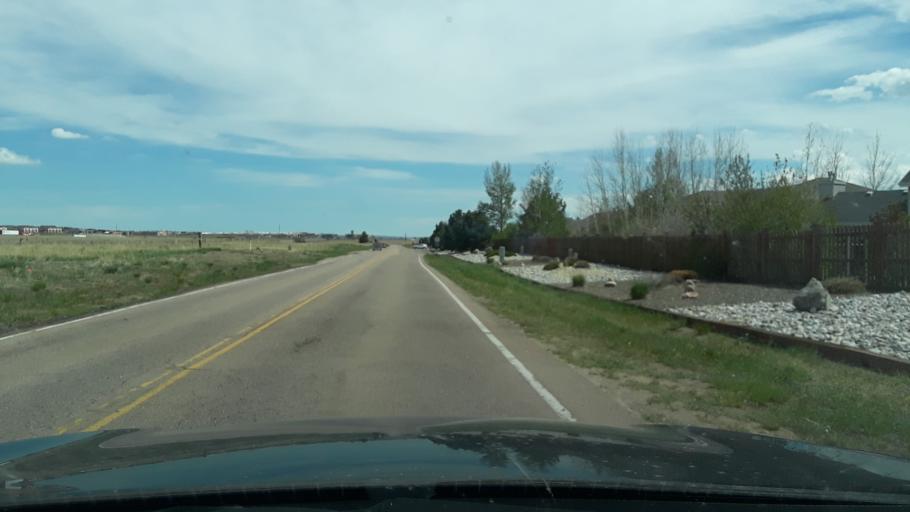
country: US
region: Colorado
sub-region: El Paso County
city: Monument
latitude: 39.0790
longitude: -104.8644
